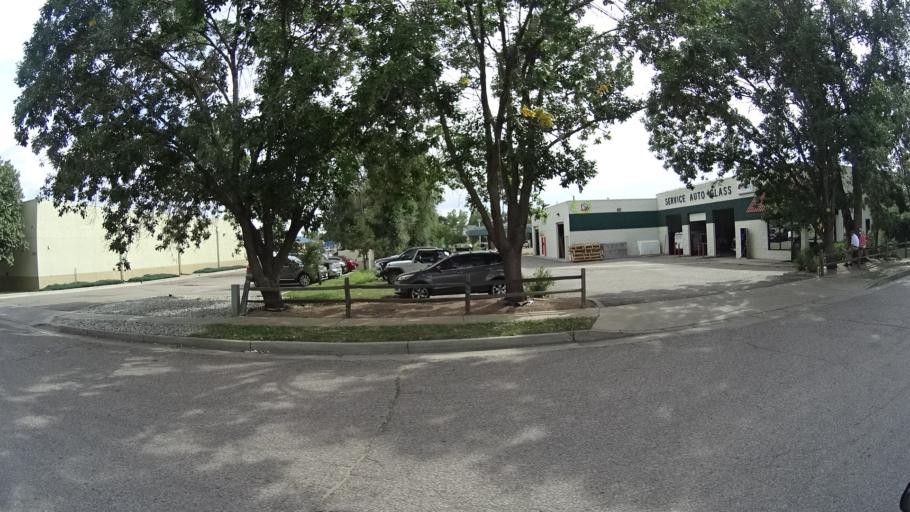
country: US
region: Colorado
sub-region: El Paso County
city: Cimarron Hills
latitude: 38.8867
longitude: -104.7582
